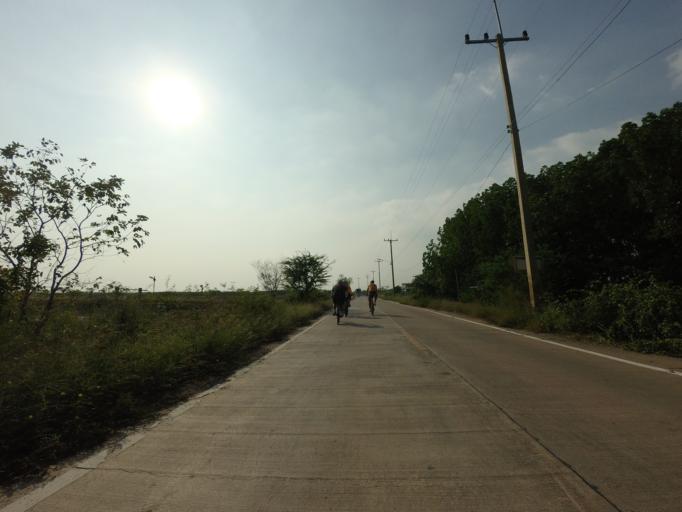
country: TH
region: Samut Sakhon
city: Samut Sakhon
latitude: 13.4985
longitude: 100.3349
